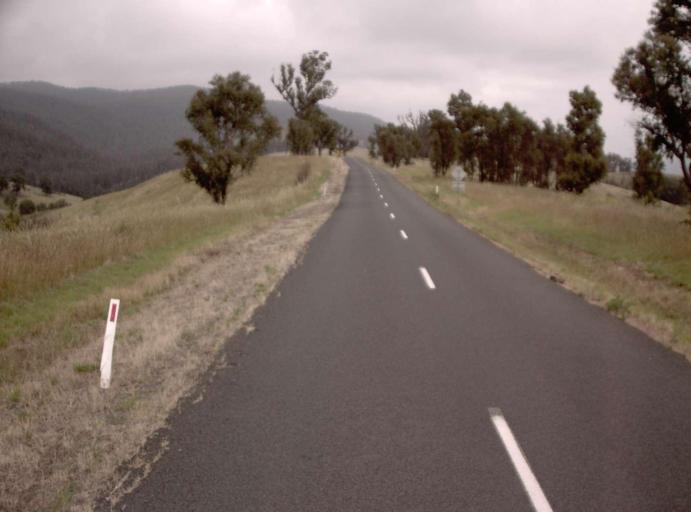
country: AU
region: Victoria
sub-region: Wellington
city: Heyfield
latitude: -37.8334
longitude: 146.6793
